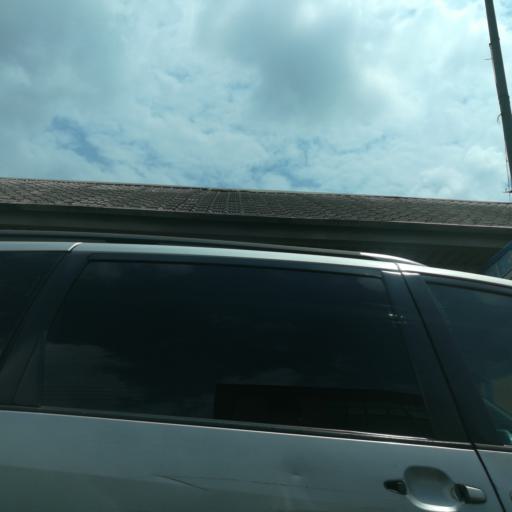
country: NG
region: Rivers
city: Port Harcourt
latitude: 4.8036
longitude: 7.0045
